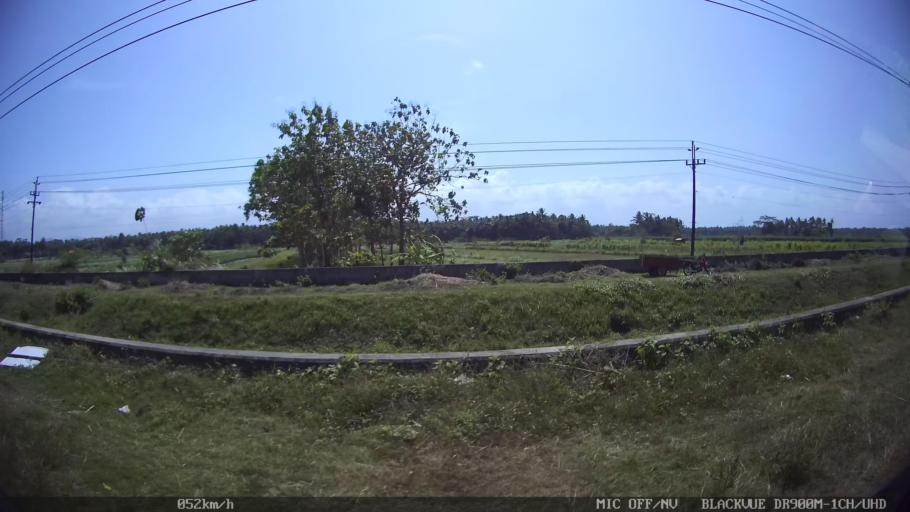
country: ID
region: Daerah Istimewa Yogyakarta
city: Srandakan
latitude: -7.9297
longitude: 110.1362
